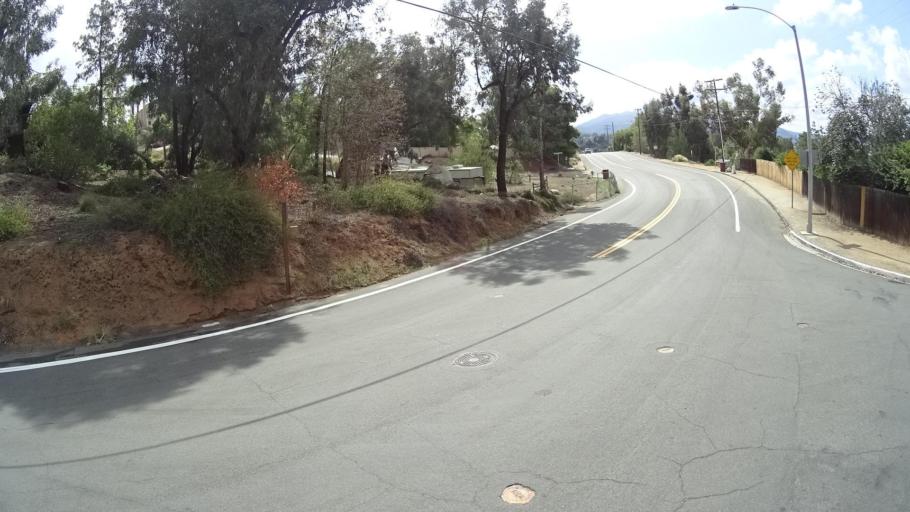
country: US
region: California
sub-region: San Diego County
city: Rancho San Diego
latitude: 32.7664
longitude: -116.9148
